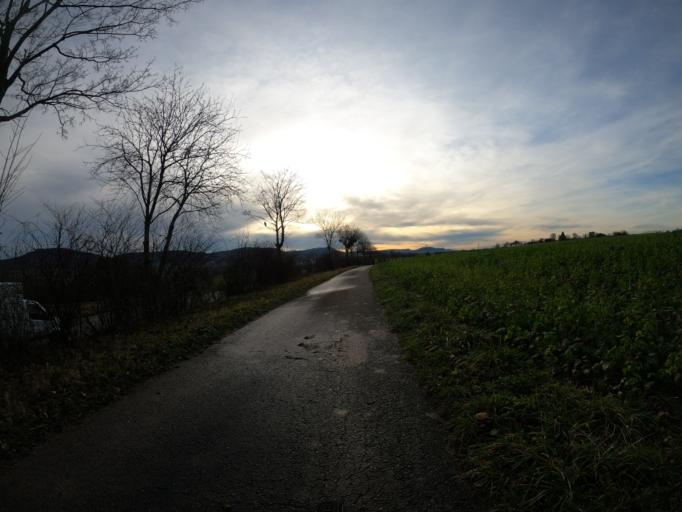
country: DE
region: Baden-Wuerttemberg
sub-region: Regierungsbezirk Stuttgart
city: Heiningen
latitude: 48.6792
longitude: 9.6628
